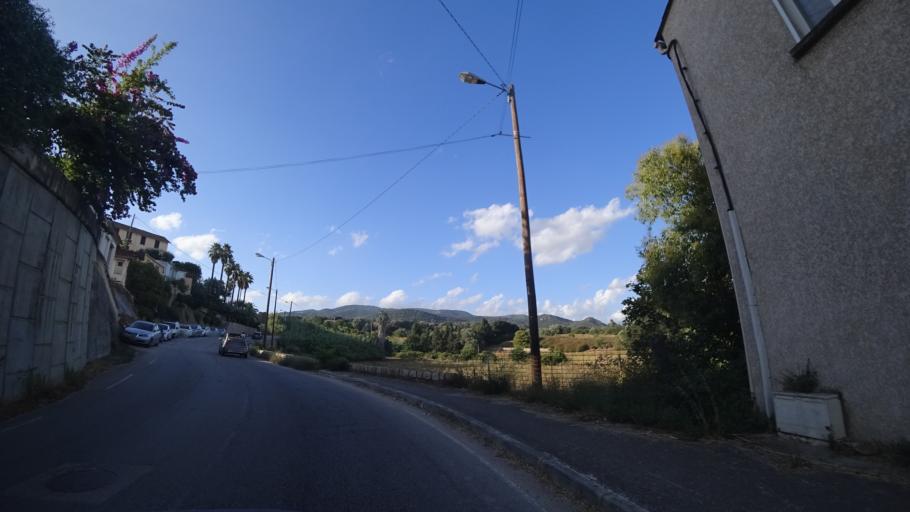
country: FR
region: Corsica
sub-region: Departement de la Corse-du-Sud
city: Ajaccio
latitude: 41.9389
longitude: 8.7383
